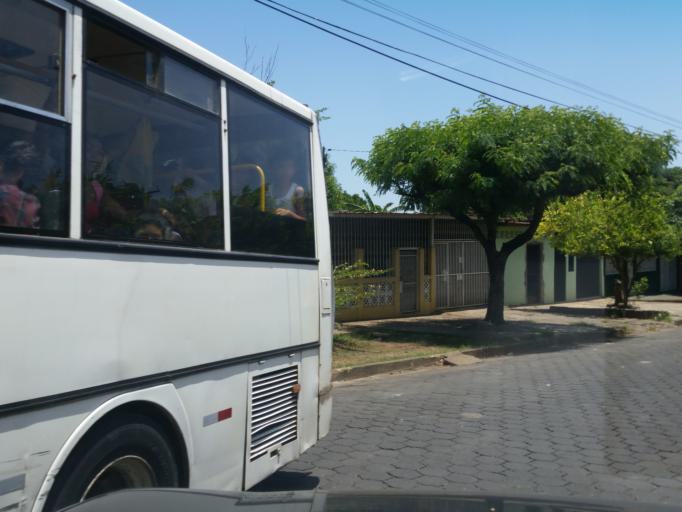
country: NI
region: Managua
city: Managua
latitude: 12.1202
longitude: -86.2406
